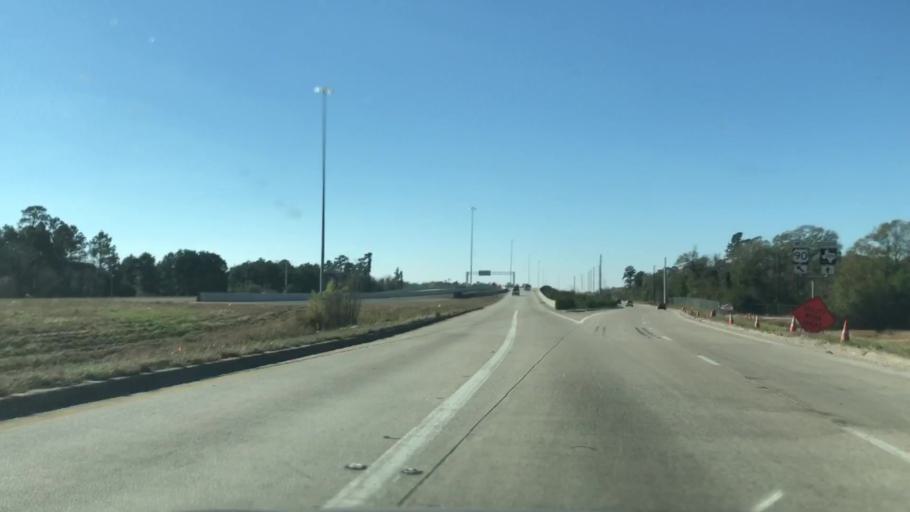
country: US
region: Texas
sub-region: Harris County
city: Jacinto City
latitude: 29.8087
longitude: -95.2149
